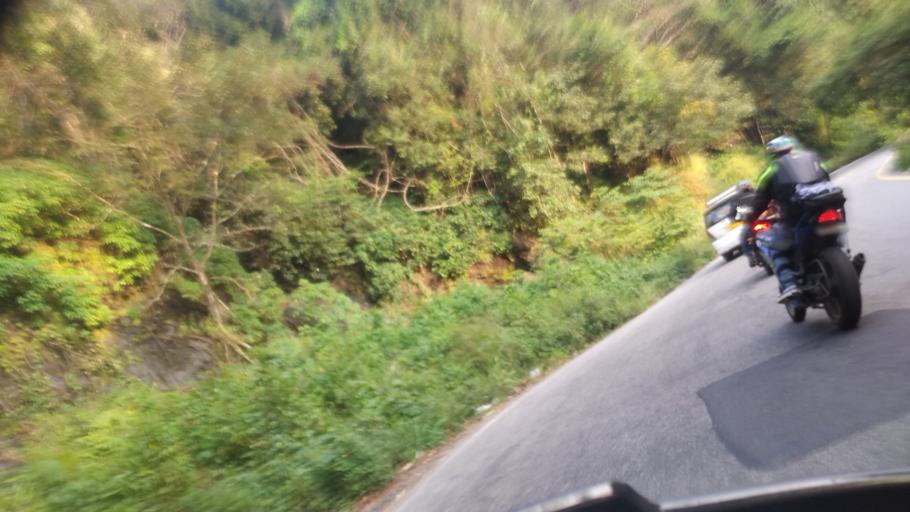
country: IN
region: Kerala
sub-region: Wayanad
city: Kalpetta
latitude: 11.5091
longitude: 76.0276
